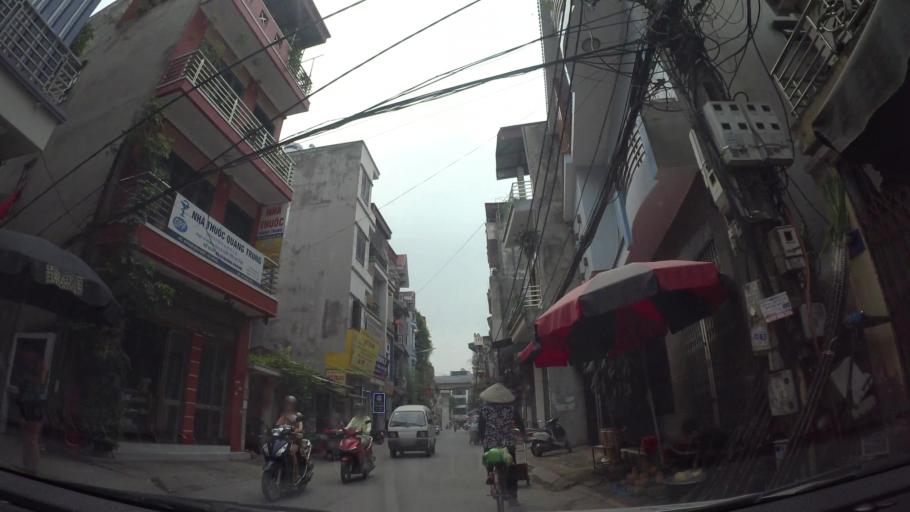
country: VN
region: Ha Noi
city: Ha Dong
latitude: 20.9652
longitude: 105.7667
